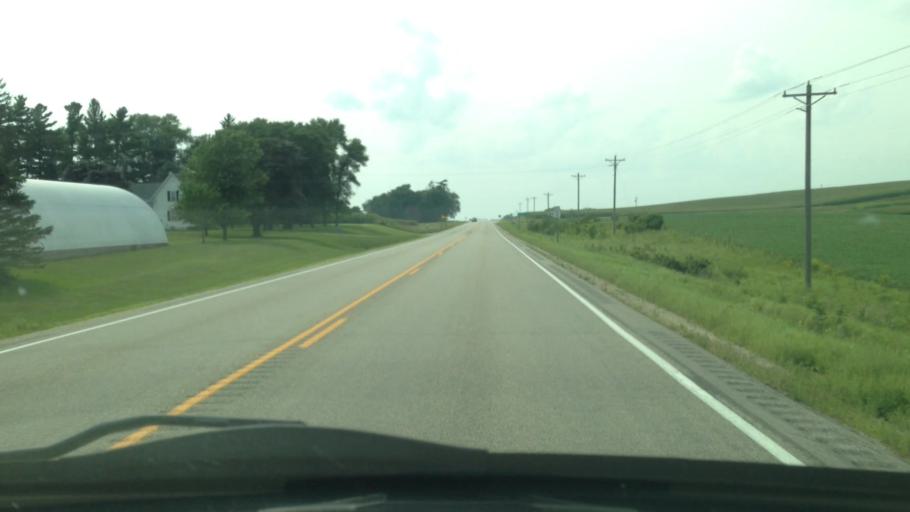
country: US
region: Minnesota
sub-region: Wabasha County
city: Elgin
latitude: 44.1654
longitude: -92.2544
